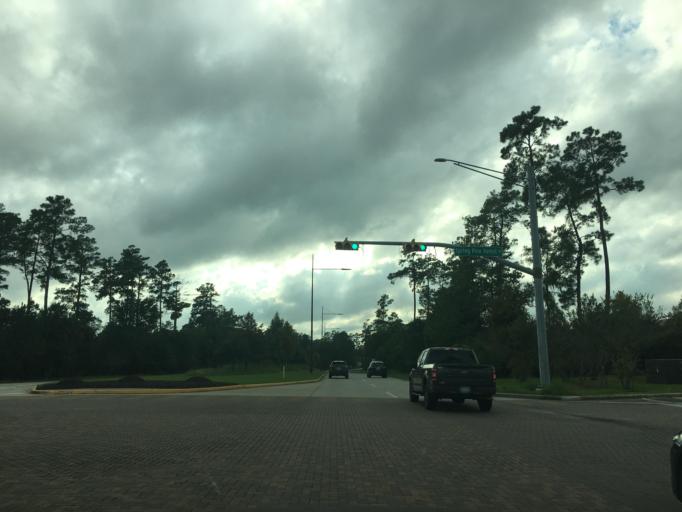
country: US
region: Texas
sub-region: Harris County
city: Spring
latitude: 30.0989
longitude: -95.4460
